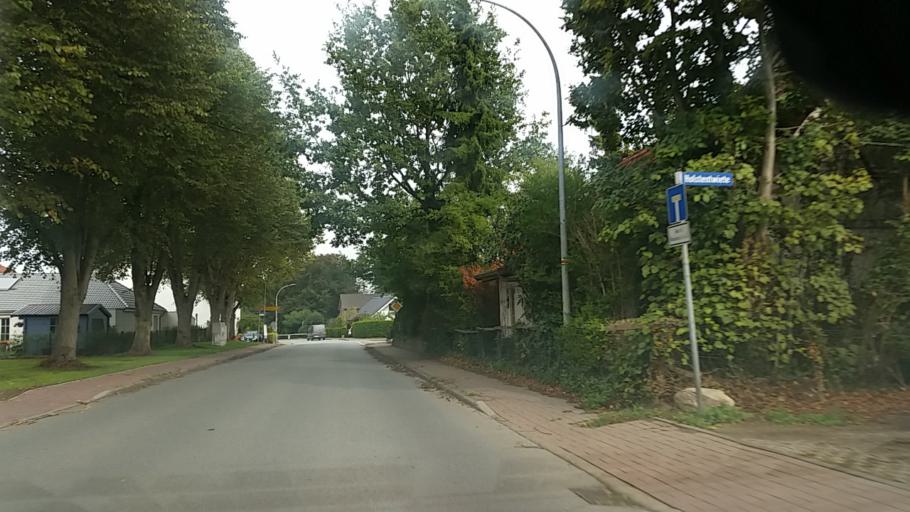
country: DE
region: Schleswig-Holstein
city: Schmalfeld
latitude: 53.8755
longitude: 9.9850
